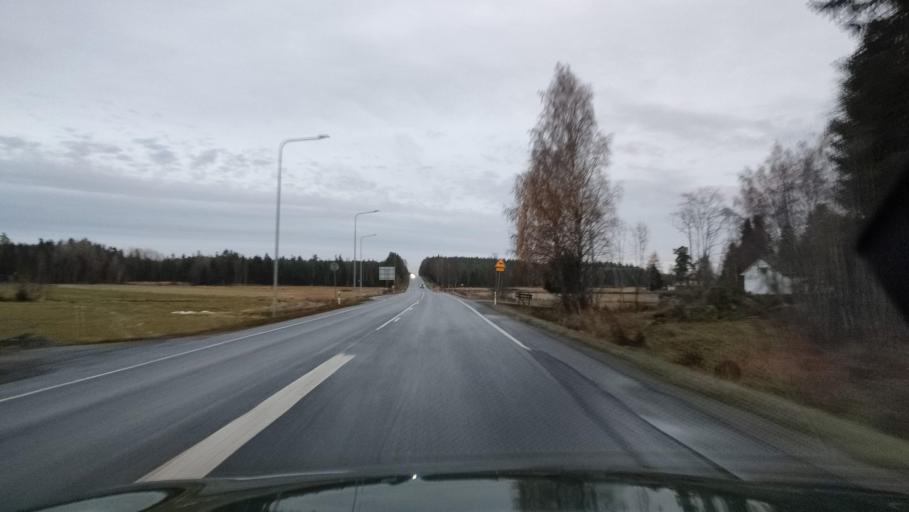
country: FI
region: Ostrobothnia
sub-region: Vaasa
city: Ristinummi
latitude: 63.0229
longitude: 21.7569
